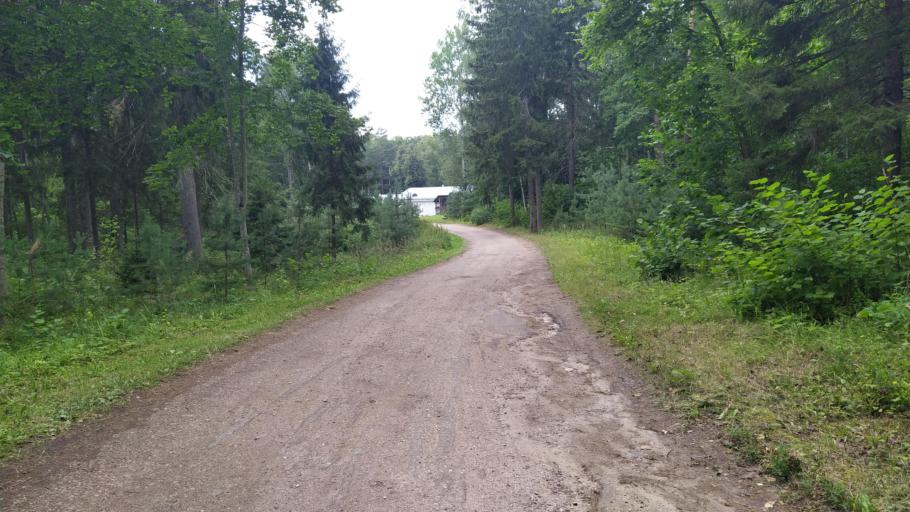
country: RU
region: Pskov
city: Pushkinskiye Gory
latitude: 57.0588
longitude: 28.9359
